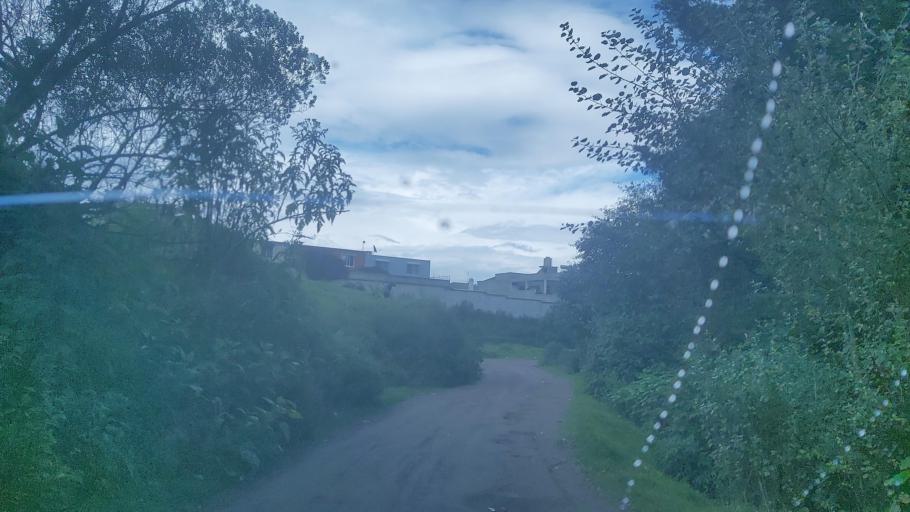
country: GT
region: Quetzaltenango
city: Quetzaltenango
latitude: 14.8528
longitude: -91.5408
